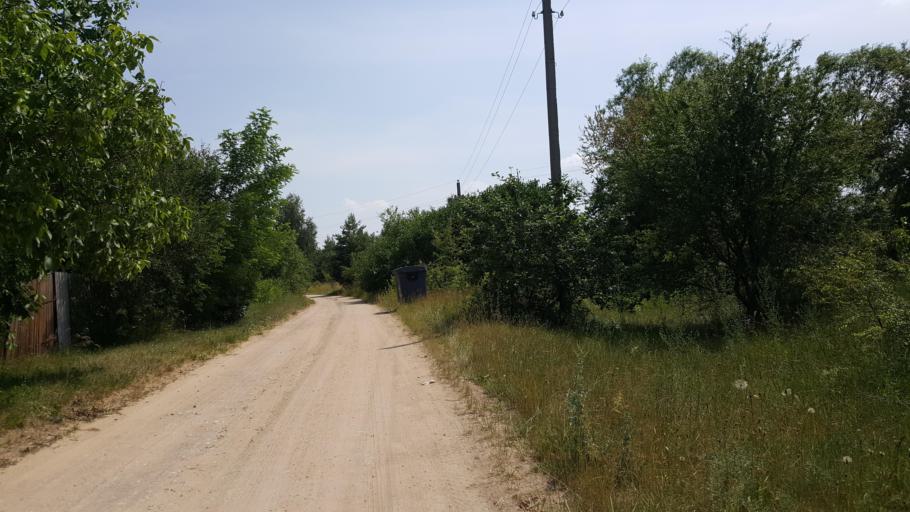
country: BY
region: Brest
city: Kamyanyets
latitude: 52.3538
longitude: 23.7544
